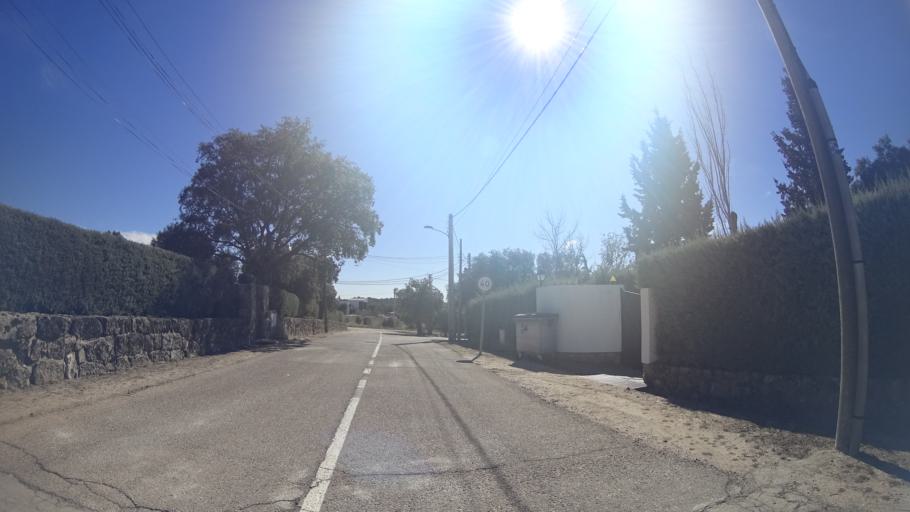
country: ES
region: Madrid
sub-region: Provincia de Madrid
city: Colmenarejo
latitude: 40.5502
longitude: -3.9930
